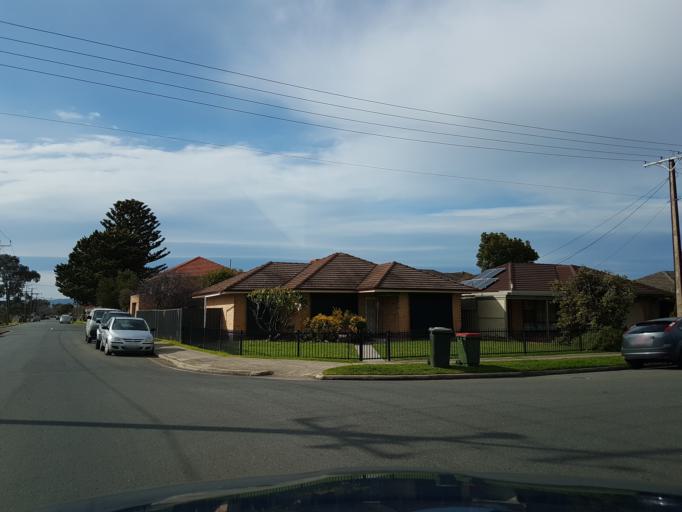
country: AU
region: South Australia
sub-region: City of West Torrens
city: Plympton
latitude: -34.9307
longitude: 138.5397
